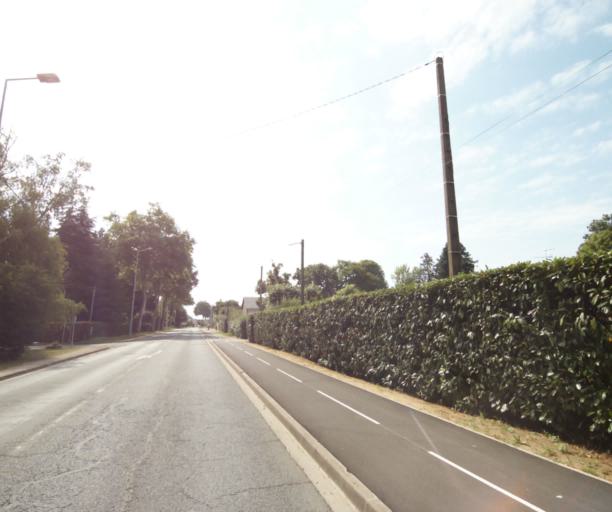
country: FR
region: Centre
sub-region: Departement du Loiret
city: Saint-Jean-le-Blanc
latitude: 47.8790
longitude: 1.9368
